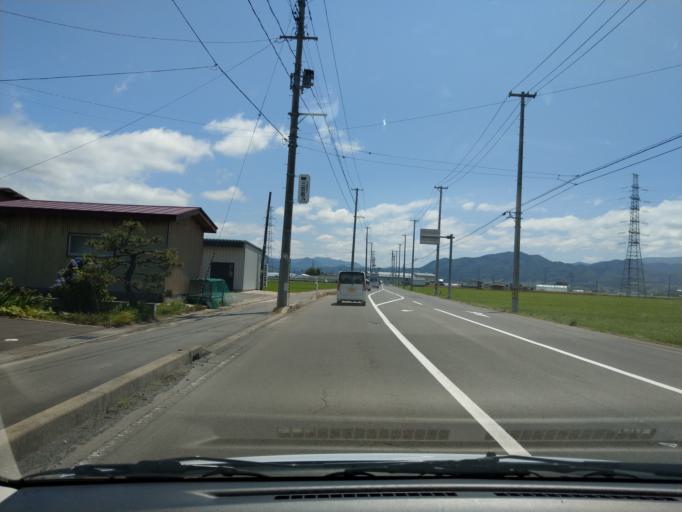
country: JP
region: Aomori
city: Kuroishi
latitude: 40.5847
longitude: 140.5510
